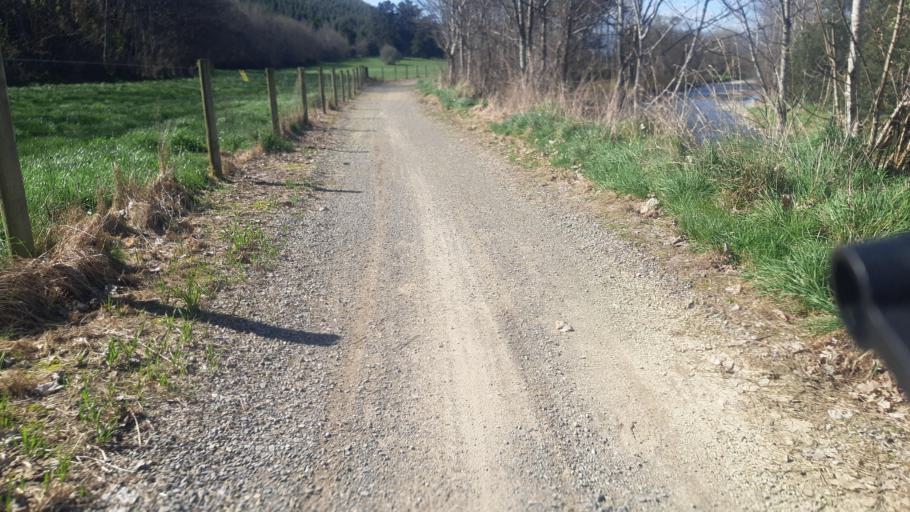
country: NZ
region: Tasman
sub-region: Tasman District
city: Wakefield
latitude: -41.4058
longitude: 173.0161
